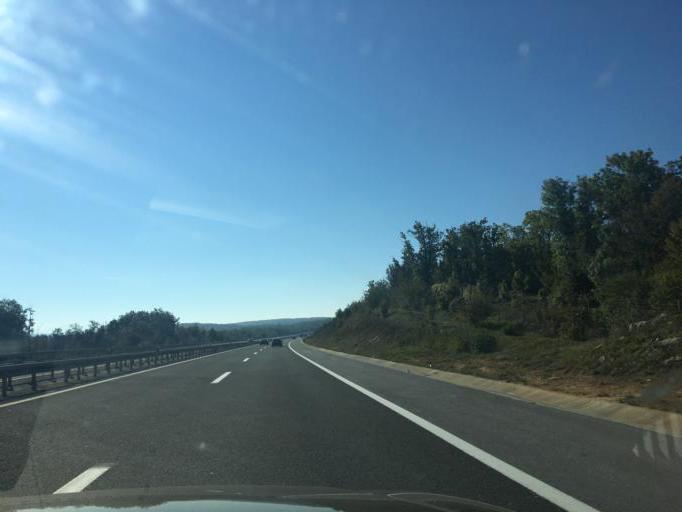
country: HR
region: Licko-Senjska
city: Gospic
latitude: 44.7318
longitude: 15.3828
